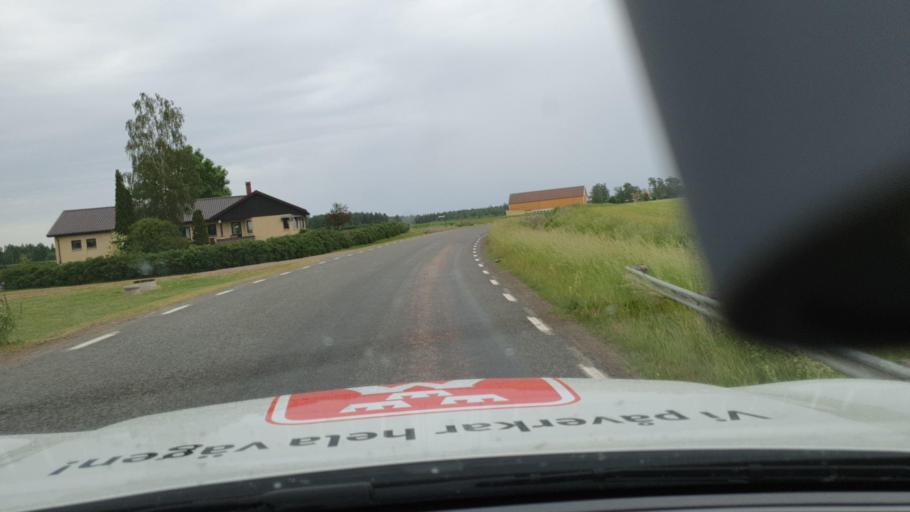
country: SE
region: Vaestra Goetaland
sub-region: Tidaholms Kommun
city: Olofstorp
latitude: 58.3323
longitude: 14.0587
